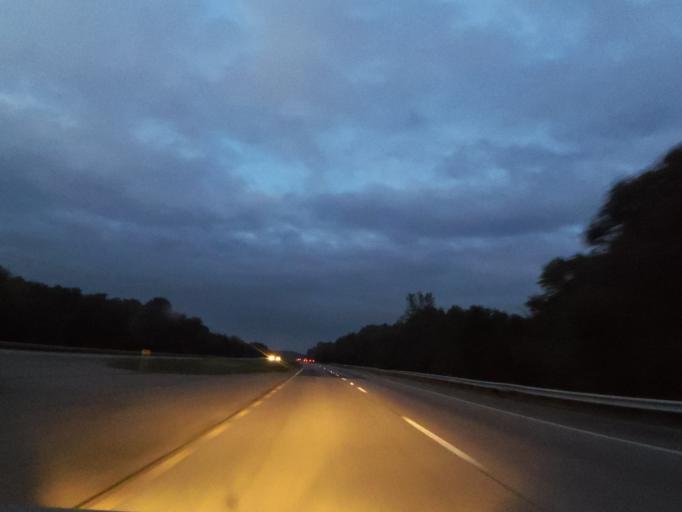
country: US
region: Alabama
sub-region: Jackson County
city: Scottsboro
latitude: 34.6182
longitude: -86.2118
